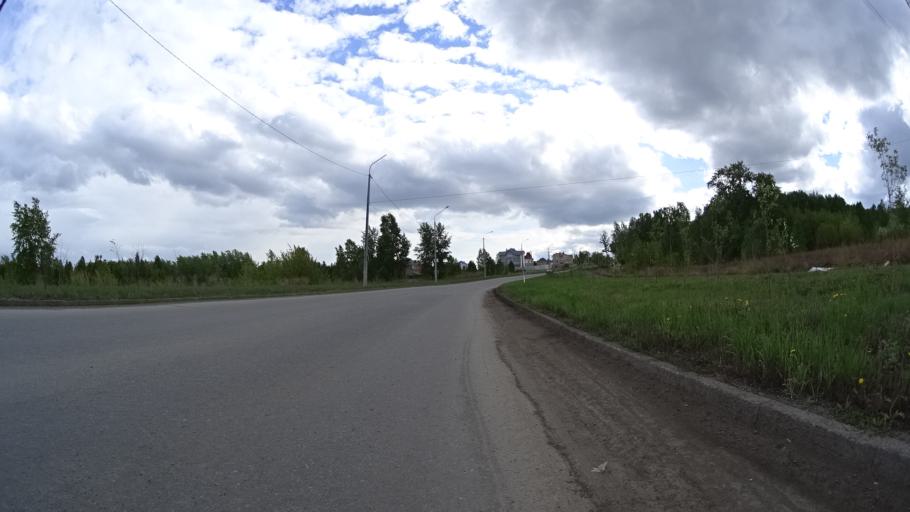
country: RU
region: Chelyabinsk
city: Sargazy
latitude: 55.1582
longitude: 61.2852
